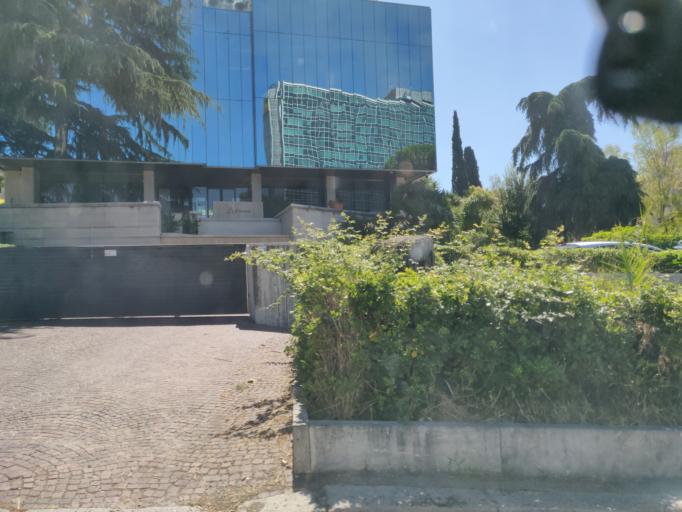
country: IT
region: Latium
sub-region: Citta metropolitana di Roma Capitale
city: Selcetta
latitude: 41.8275
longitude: 12.4734
